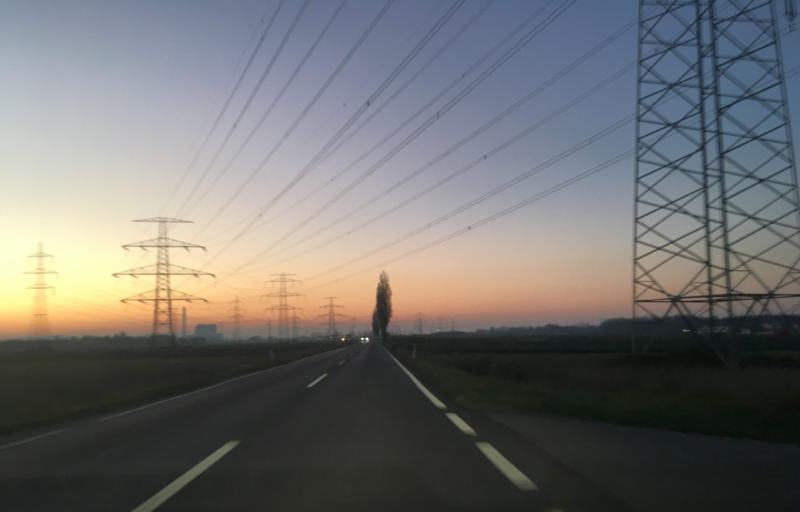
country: AT
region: Lower Austria
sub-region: Politischer Bezirk Tulln
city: Langenrohr
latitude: 48.3242
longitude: 15.9793
